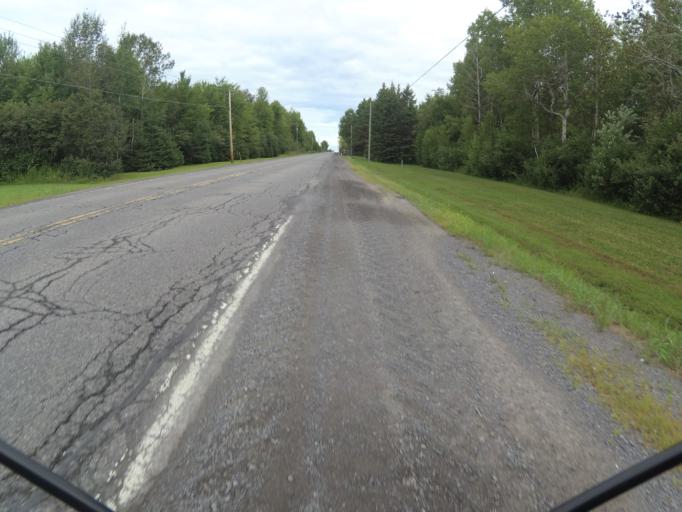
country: CA
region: Ontario
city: Bourget
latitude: 45.3731
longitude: -75.2687
